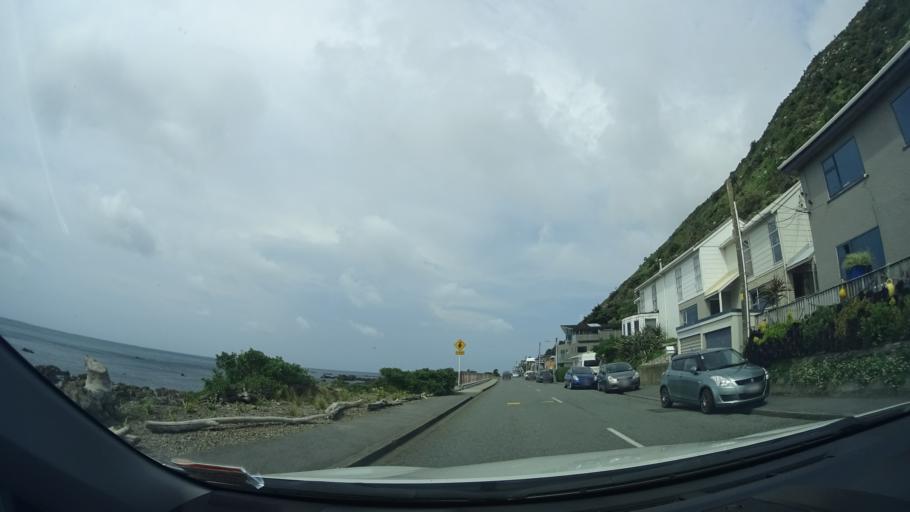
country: NZ
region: Wellington
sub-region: Wellington City
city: Brooklyn
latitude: -41.3461
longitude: 174.7559
